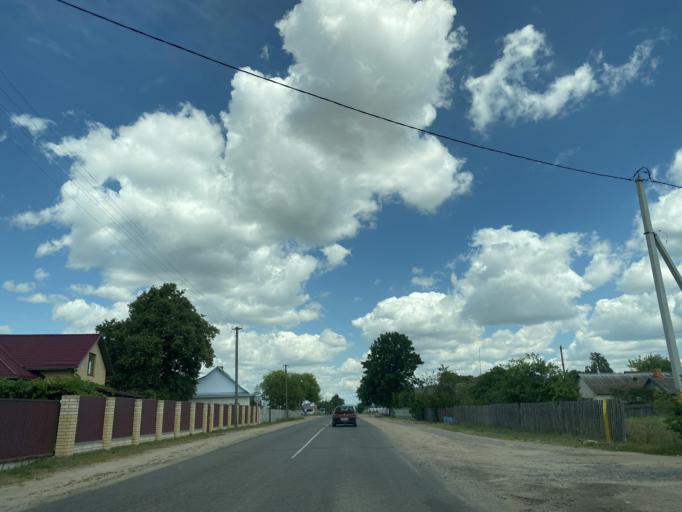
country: BY
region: Brest
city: Ivanava
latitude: 52.1668
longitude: 25.5498
